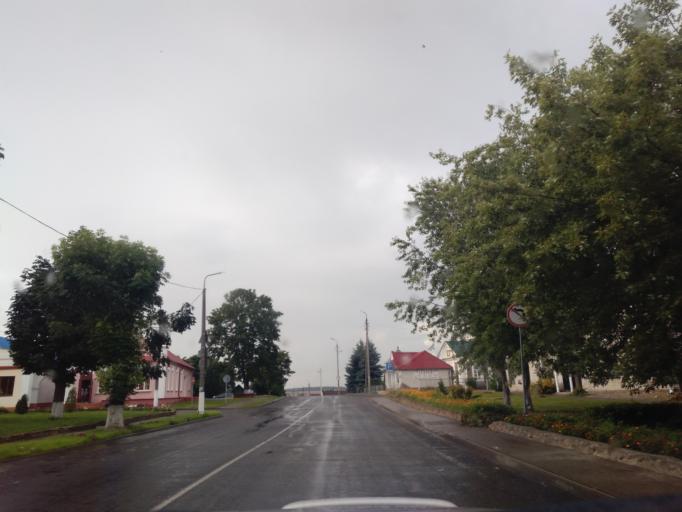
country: BY
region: Minsk
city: Kapyl'
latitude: 53.1524
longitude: 27.0913
